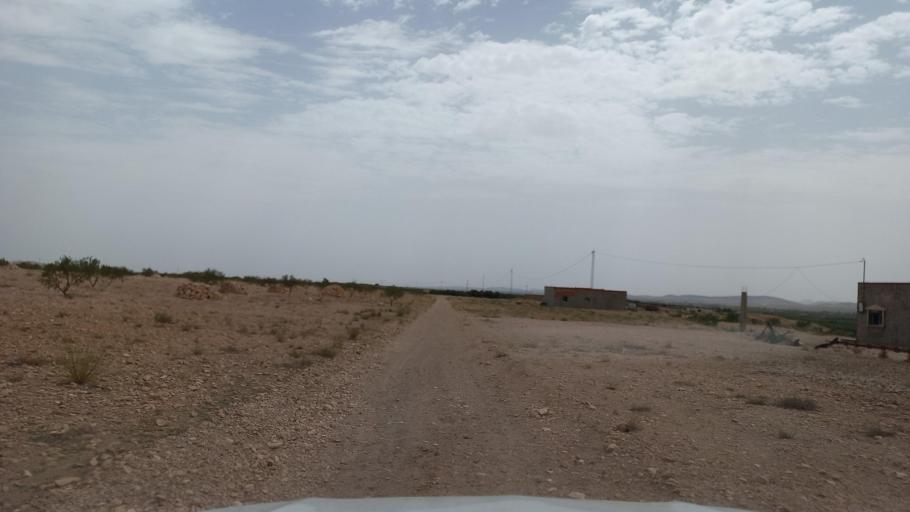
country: TN
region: Al Qasrayn
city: Kasserine
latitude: 35.2915
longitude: 9.0018
